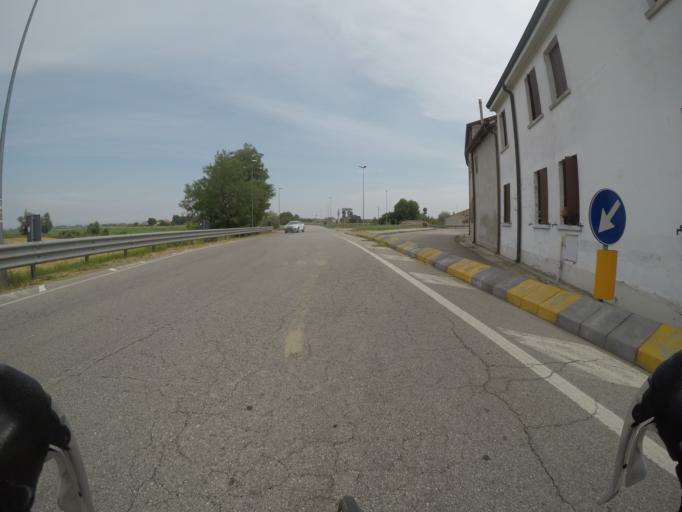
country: IT
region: Veneto
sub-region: Provincia di Rovigo
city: Costa di Rovigo
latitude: 45.0492
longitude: 11.6879
